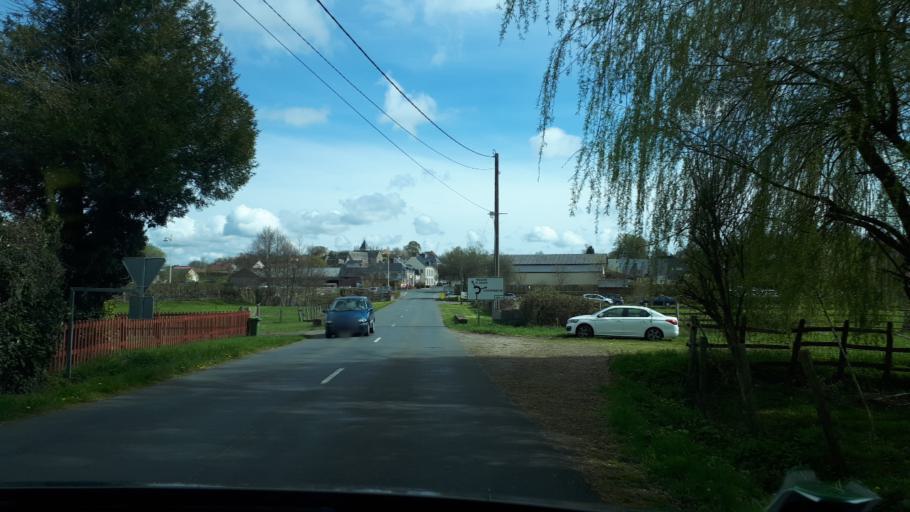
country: FR
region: Pays de la Loire
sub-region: Departement de la Sarthe
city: Le Grand-Luce
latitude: 47.8637
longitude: 0.4771
